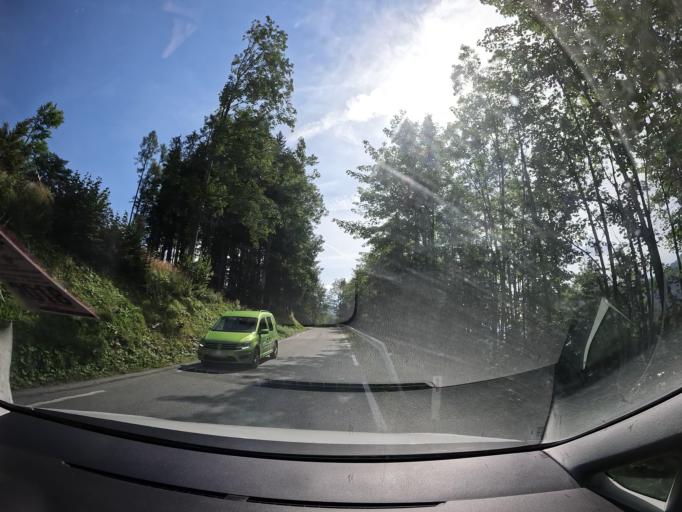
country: AT
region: Carinthia
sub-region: Politischer Bezirk Sankt Veit an der Glan
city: Liebenfels
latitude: 46.7094
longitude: 14.2690
